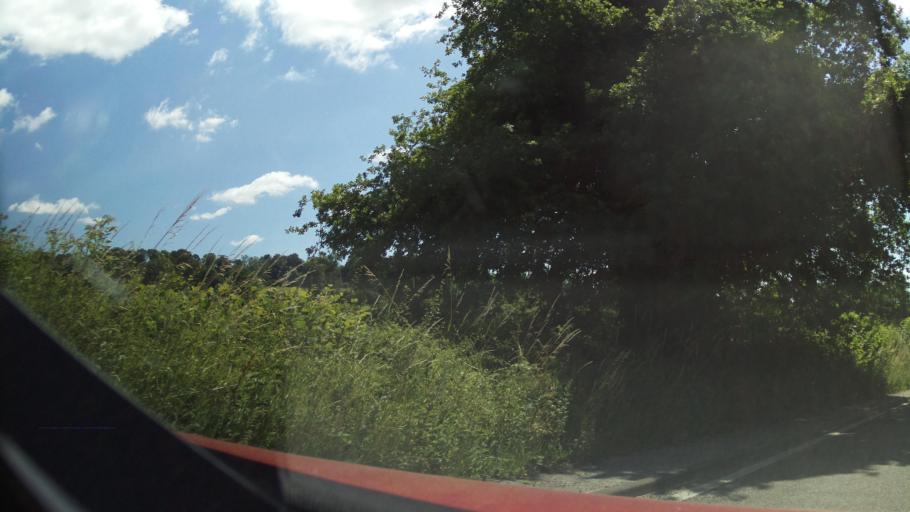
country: GB
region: England
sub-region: Derbyshire
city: Ashbourne
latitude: 53.0371
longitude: -1.7339
